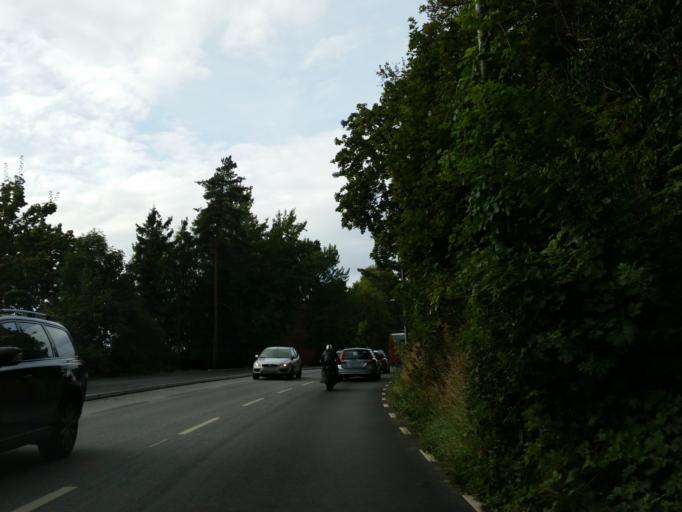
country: SE
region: Stockholm
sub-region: Sollentuna Kommun
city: Sollentuna
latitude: 59.4431
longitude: 17.9472
